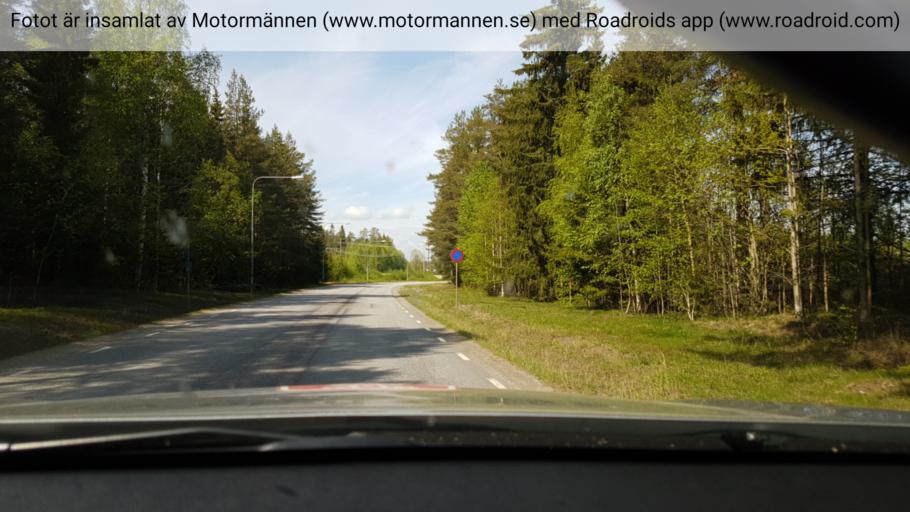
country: SE
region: Vaesterbotten
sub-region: Umea Kommun
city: Roback
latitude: 63.8165
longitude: 20.1809
